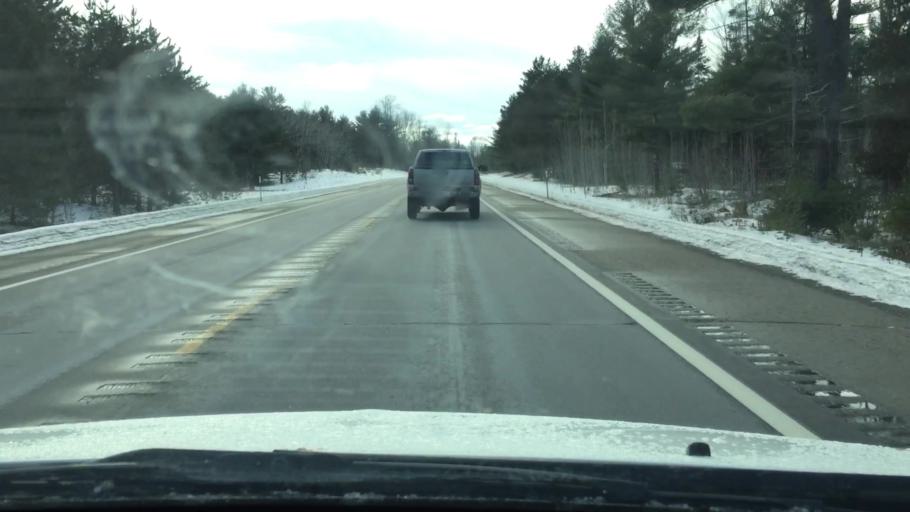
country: US
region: Michigan
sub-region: Kalkaska County
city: Kalkaska
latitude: 44.6500
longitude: -85.2689
